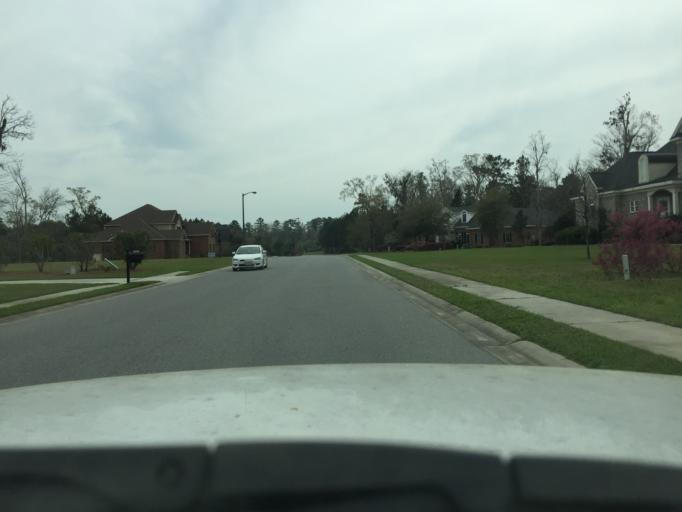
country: US
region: Georgia
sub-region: Chatham County
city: Pooler
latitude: 32.0522
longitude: -81.2411
